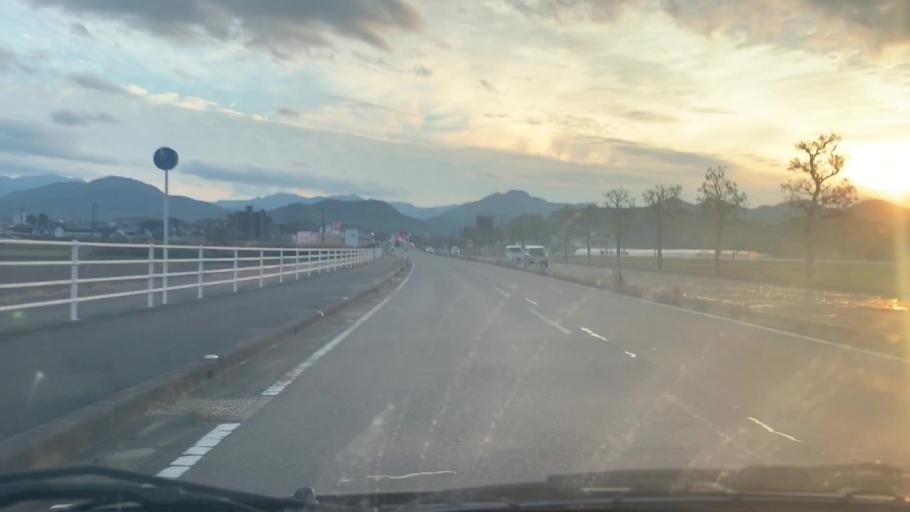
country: JP
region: Saga Prefecture
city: Kashima
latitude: 33.1174
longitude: 130.0898
